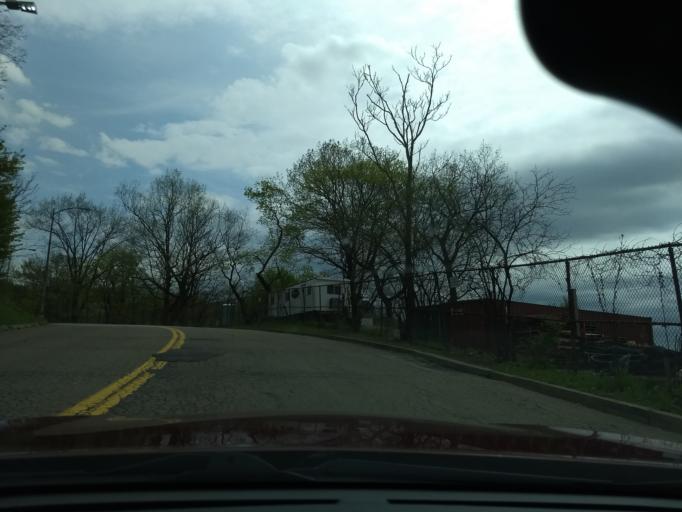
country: US
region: Pennsylvania
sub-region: Allegheny County
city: Sharpsburg
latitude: 40.4843
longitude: -79.9170
